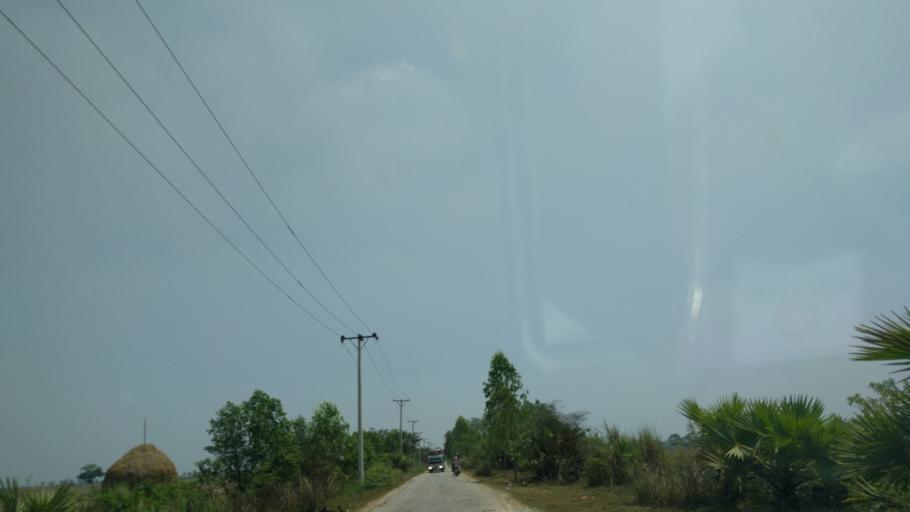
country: MM
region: Mon
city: Martaban
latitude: 16.5857
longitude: 97.6655
